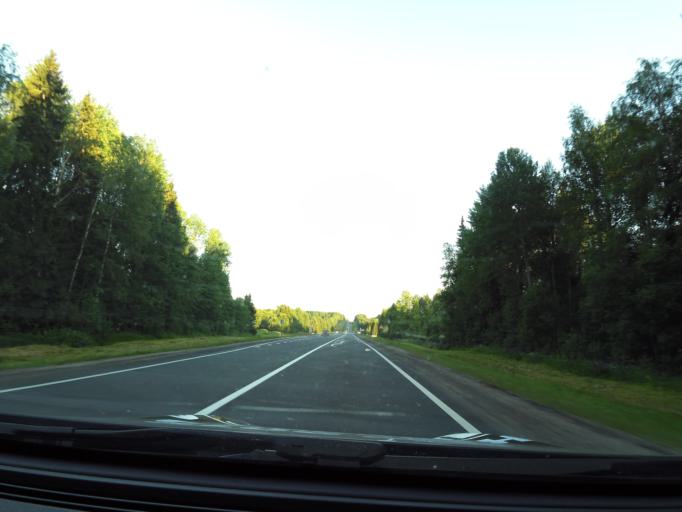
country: RU
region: Vologda
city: Gryazovets
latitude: 58.6852
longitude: 40.3047
